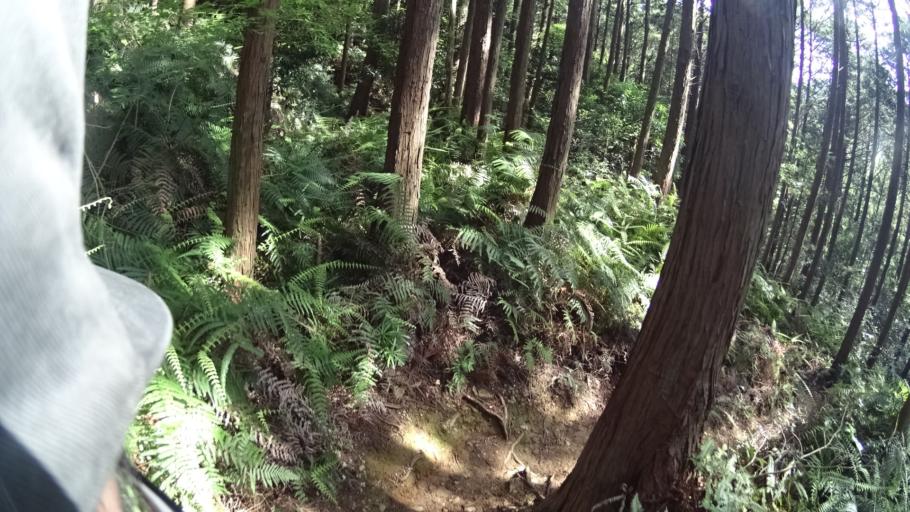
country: JP
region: Shizuoka
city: Kosai-shi
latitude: 34.7775
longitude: 137.4933
